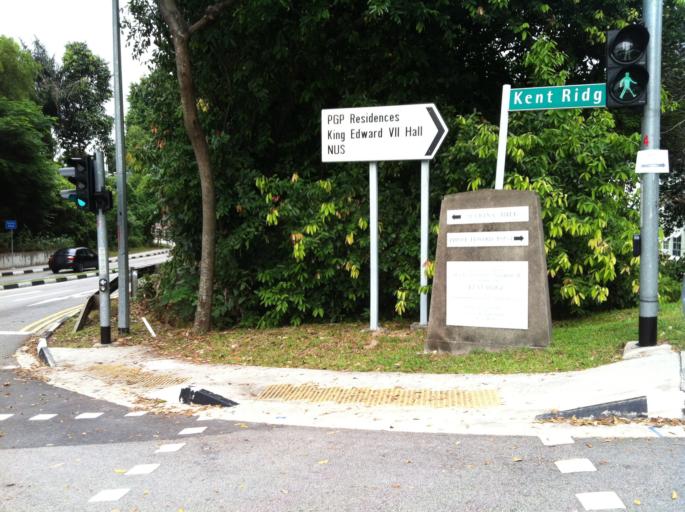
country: SG
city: Singapore
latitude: 1.2916
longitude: 103.7834
